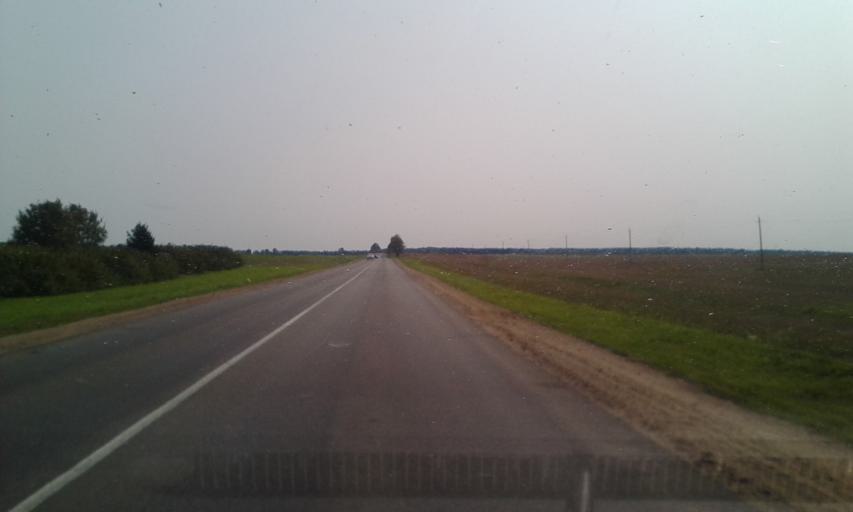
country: BY
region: Minsk
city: Hatava
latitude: 53.8288
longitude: 27.6173
